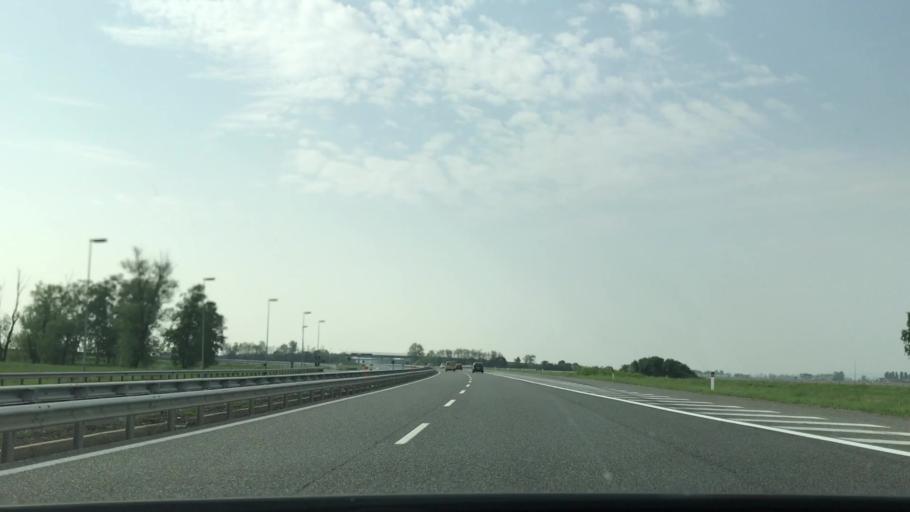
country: IT
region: Piedmont
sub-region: Provincia di Vercelli
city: Stroppiana
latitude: 45.2446
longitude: 8.4671
